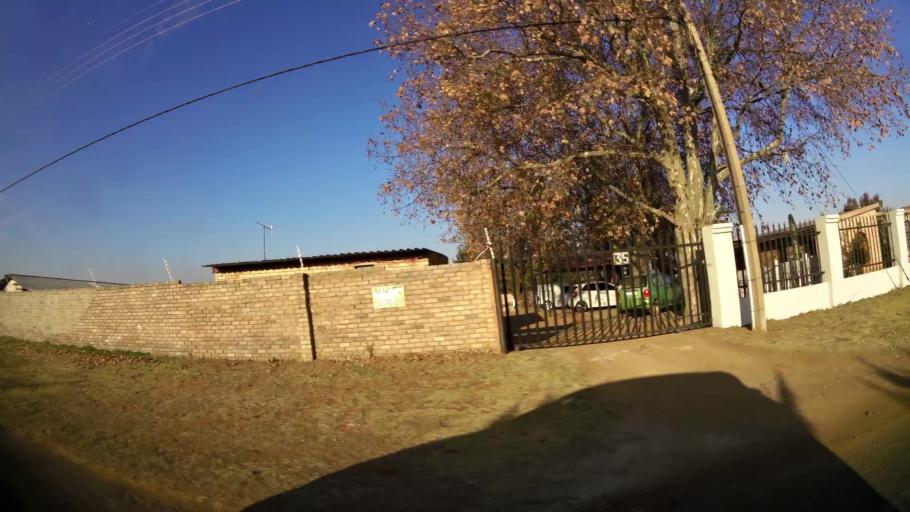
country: ZA
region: Gauteng
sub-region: West Rand District Municipality
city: Randfontein
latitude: -26.2112
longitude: 27.6430
